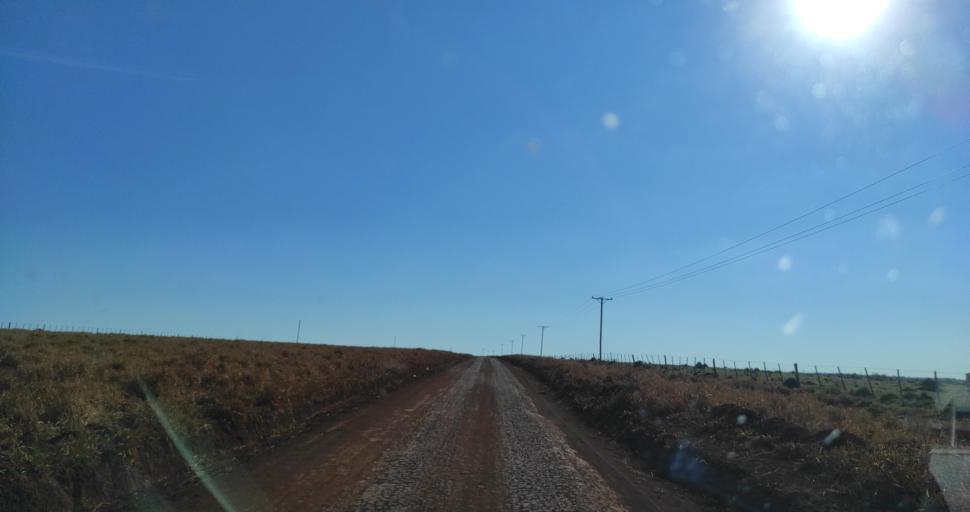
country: PY
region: Itapua
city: San Juan del Parana
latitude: -27.4362
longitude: -56.0692
